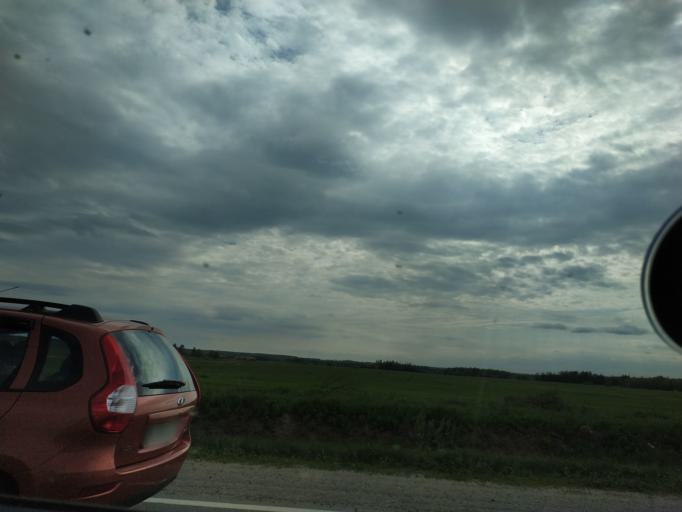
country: RU
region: Moskovskaya
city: Malyshevo
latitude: 55.4984
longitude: 38.3037
